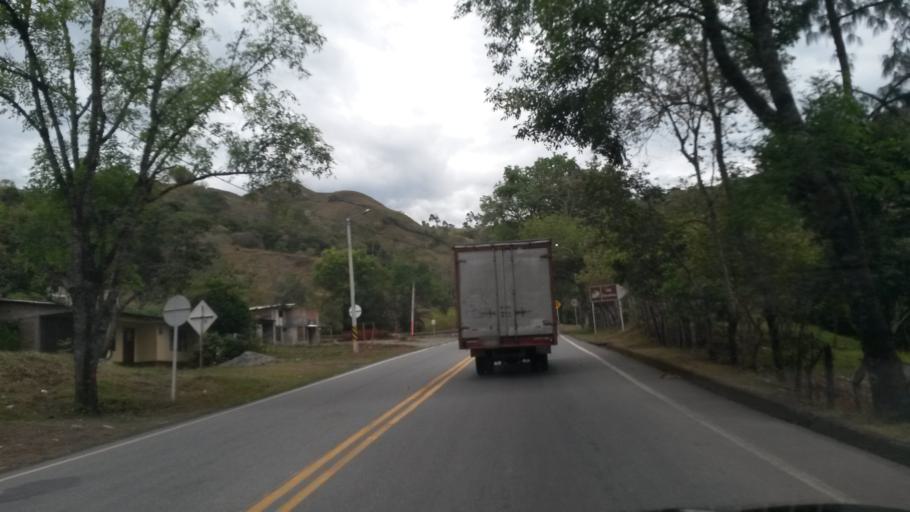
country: CO
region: Cauca
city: Rosas
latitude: 2.2625
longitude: -76.7393
